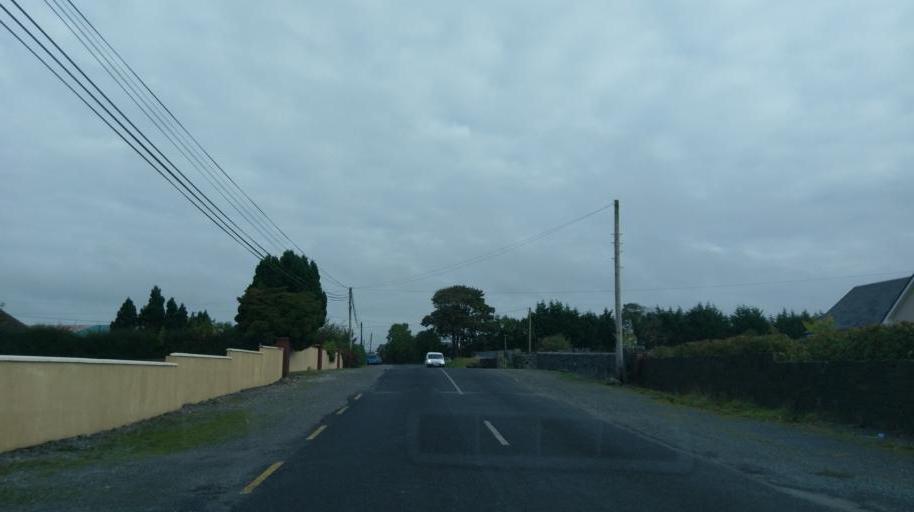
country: IE
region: Connaught
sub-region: County Galway
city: Athenry
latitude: 53.3473
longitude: -8.7096
